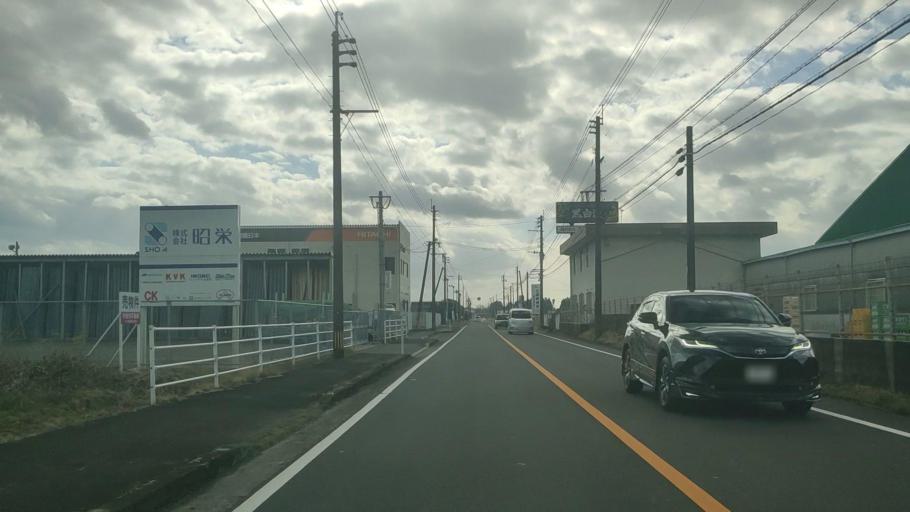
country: JP
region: Kagoshima
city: Kajiki
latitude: 31.7830
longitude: 130.7050
